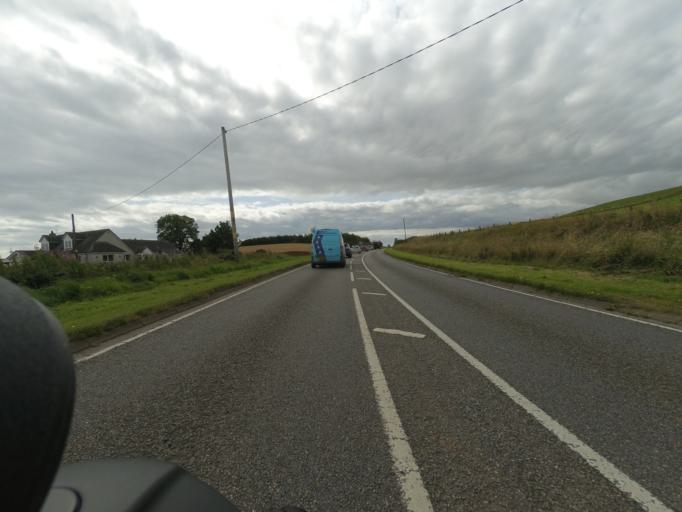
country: GB
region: Scotland
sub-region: Aberdeenshire
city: Inverbervie
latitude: 56.8781
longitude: -2.2569
